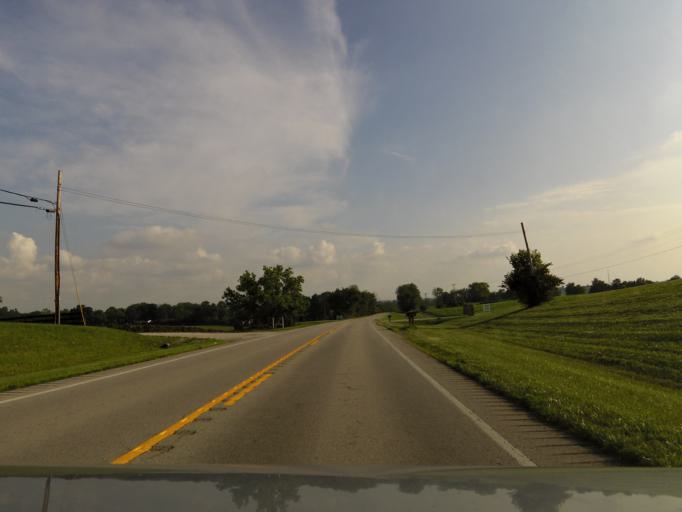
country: US
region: Kentucky
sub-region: Harrison County
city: Cynthiana
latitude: 38.3223
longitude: -84.3023
